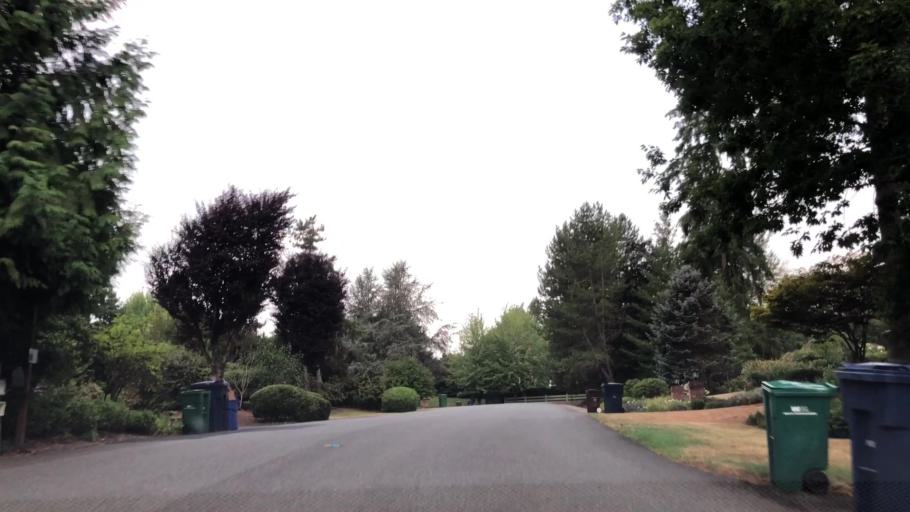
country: US
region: Washington
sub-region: King County
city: Cottage Lake
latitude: 47.7187
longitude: -122.0979
